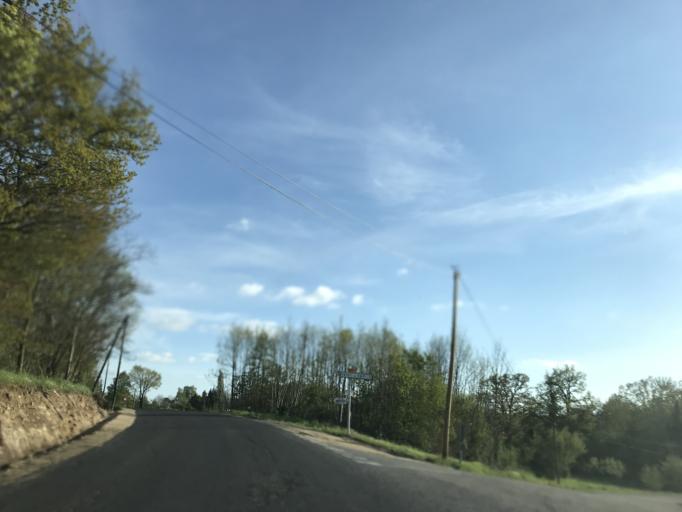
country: FR
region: Auvergne
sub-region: Departement du Puy-de-Dome
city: Montaigut
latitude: 45.6798
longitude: 3.4264
